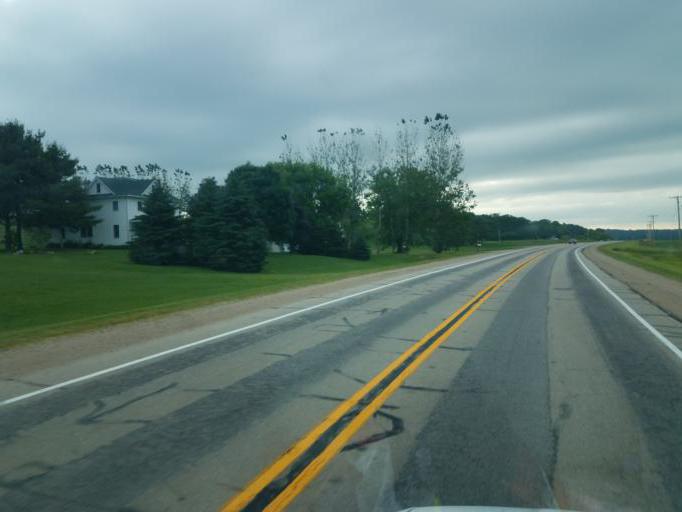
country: US
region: Wisconsin
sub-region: Vernon County
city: Hillsboro
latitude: 43.6791
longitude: -90.2958
